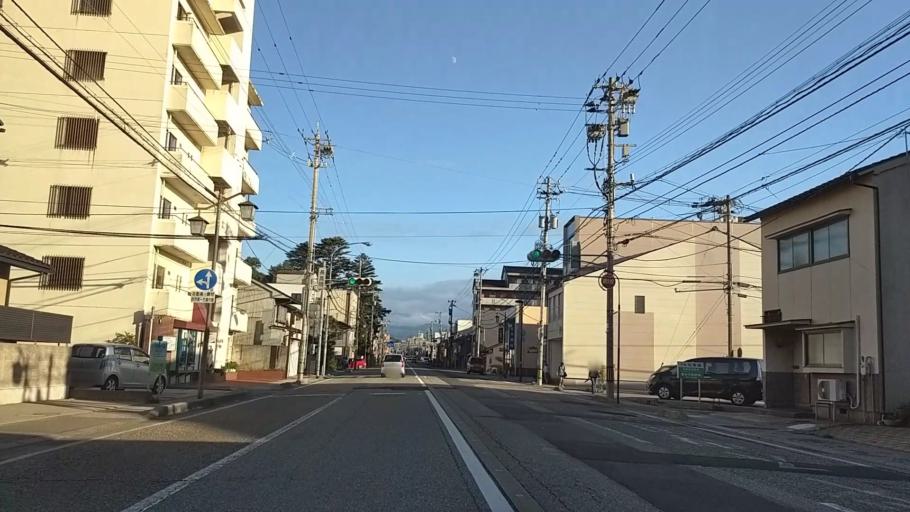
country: JP
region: Ishikawa
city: Nonoichi
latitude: 36.5484
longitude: 136.6574
